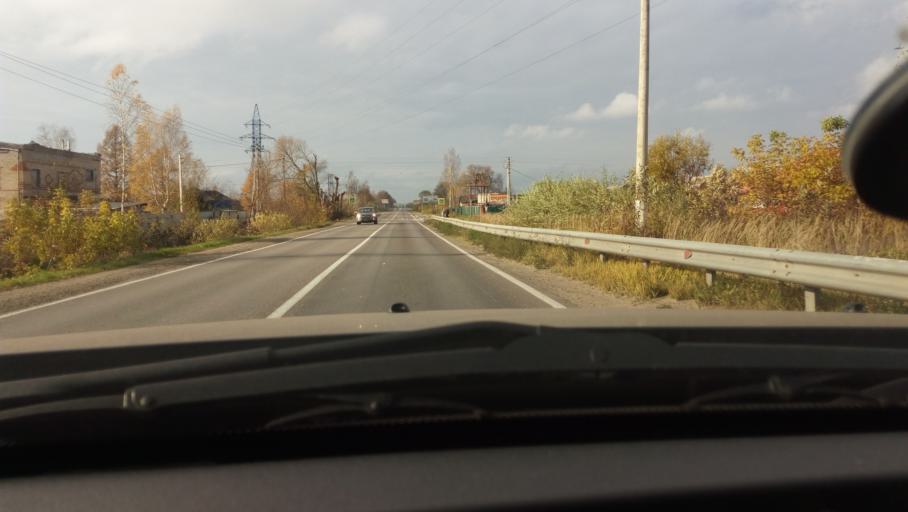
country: RU
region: Moskovskaya
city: Rakhmanovo
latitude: 55.7475
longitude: 38.5801
